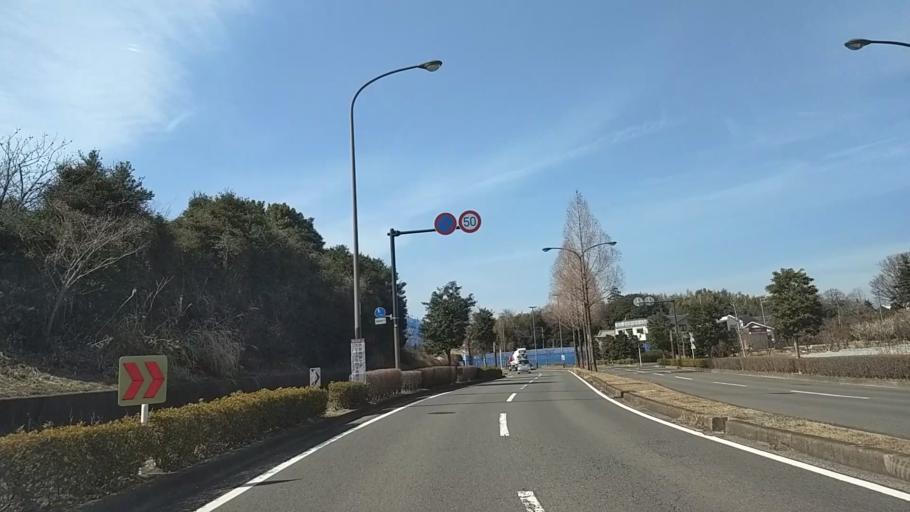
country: JP
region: Kanagawa
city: Fujisawa
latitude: 35.3925
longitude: 139.4248
